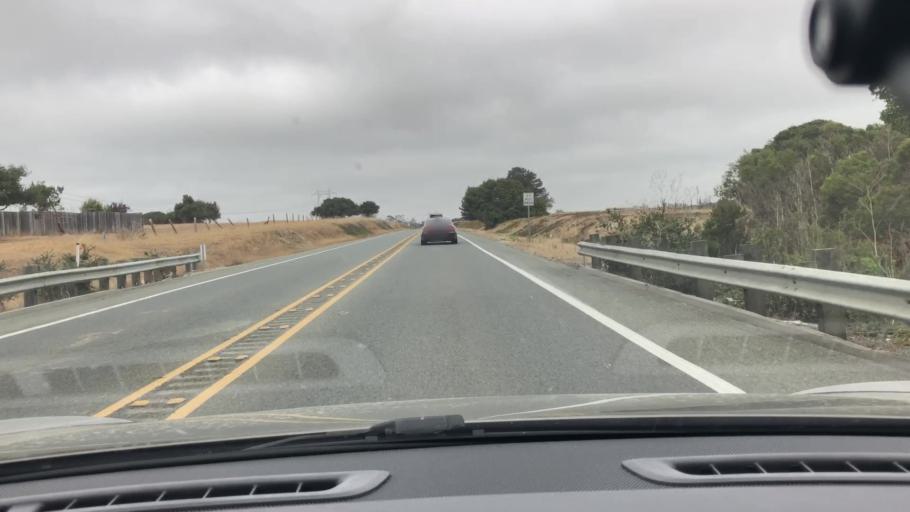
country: US
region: California
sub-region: Monterey County
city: Prunedale
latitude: 36.7812
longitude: -121.6992
